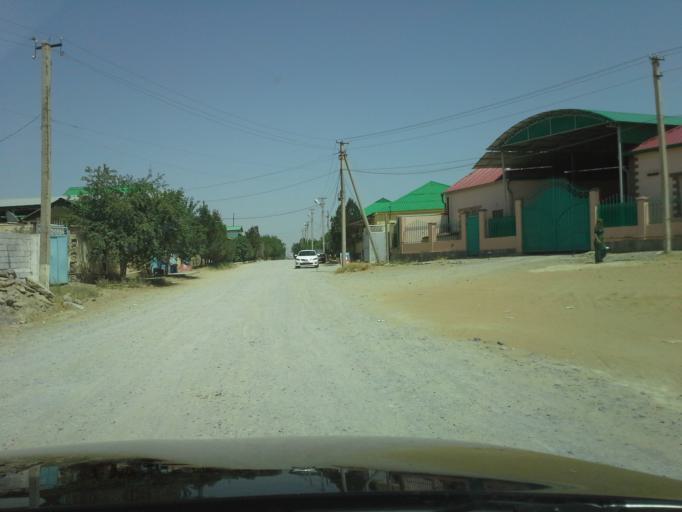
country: TM
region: Ahal
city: Ashgabat
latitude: 38.0029
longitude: 58.4066
